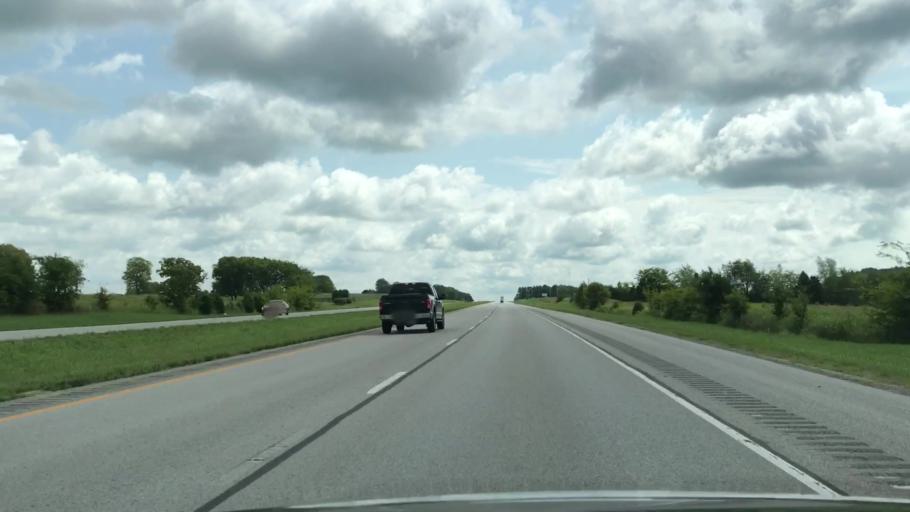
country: US
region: Kentucky
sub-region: Logan County
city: Auburn
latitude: 36.8910
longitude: -86.6362
